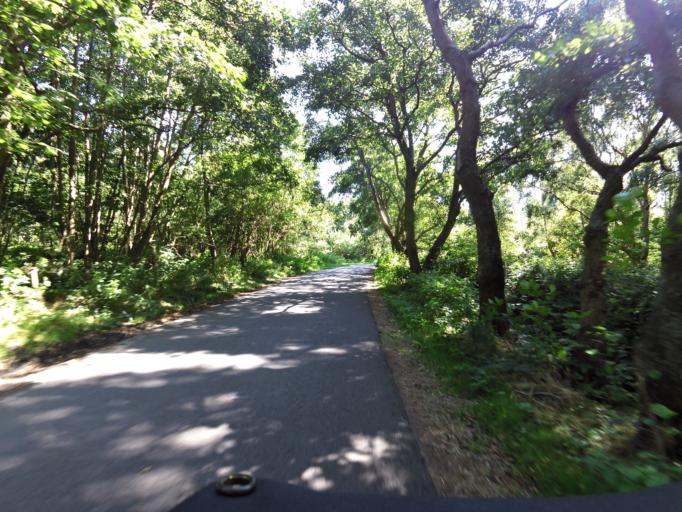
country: NL
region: Zeeland
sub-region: Schouwen-Duiveland
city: Renesse
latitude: 51.7283
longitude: 3.7447
